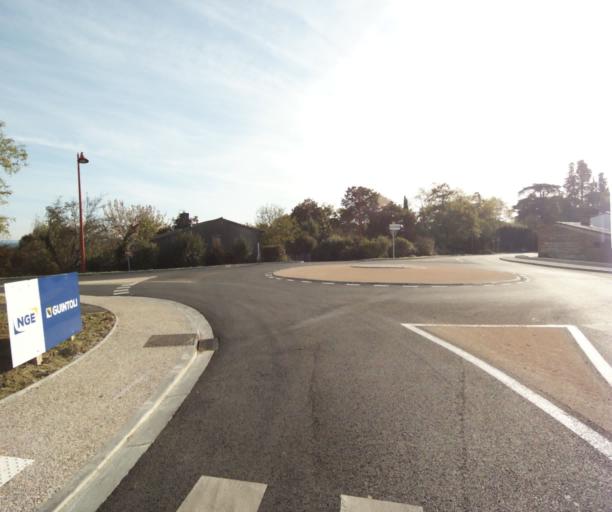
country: FR
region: Midi-Pyrenees
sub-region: Departement de la Haute-Garonne
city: Villemur-sur-Tarn
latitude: 43.9031
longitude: 1.4931
